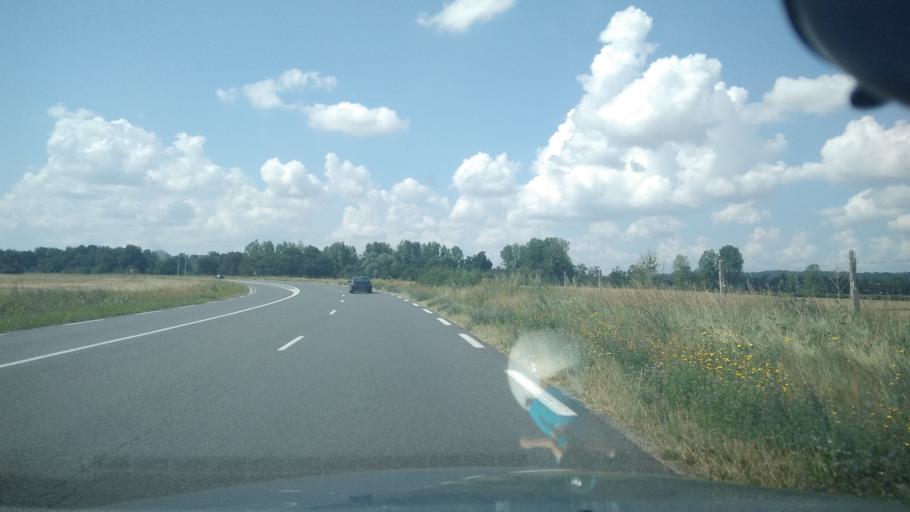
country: FR
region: Centre
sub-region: Departement d'Indre-et-Loire
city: La Celle-Saint-Avant
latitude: 47.0015
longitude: 0.5955
